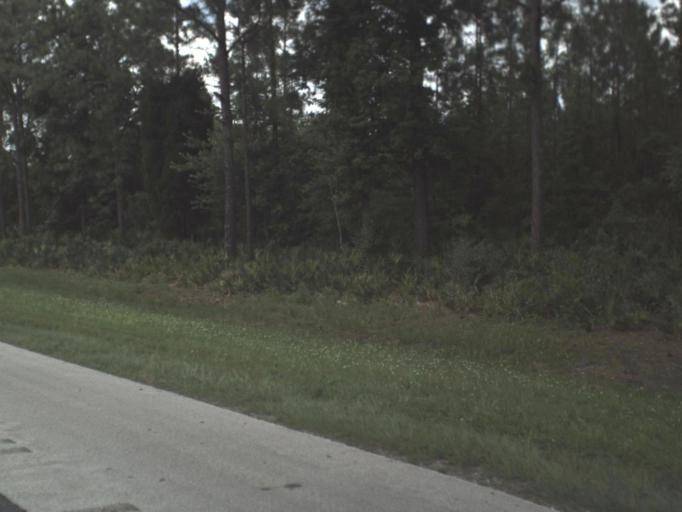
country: US
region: Florida
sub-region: Saint Johns County
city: Saint Augustine South
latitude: 29.8498
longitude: -81.3910
